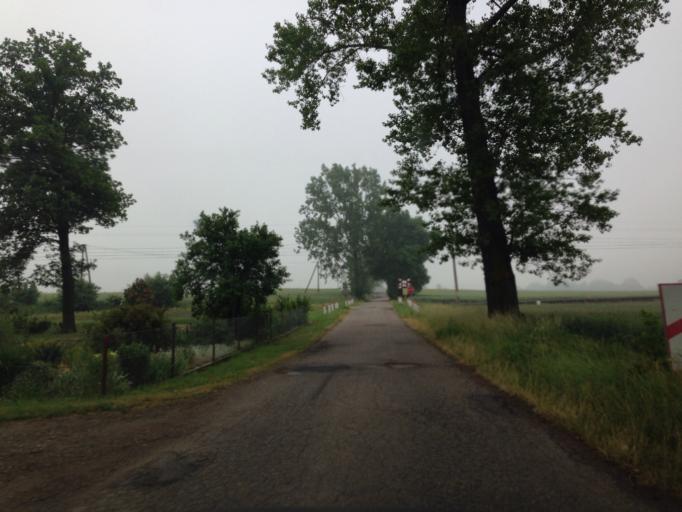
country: PL
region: Kujawsko-Pomorskie
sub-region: Powiat brodnicki
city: Jablonowo Pomorskie
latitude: 53.4067
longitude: 19.2206
